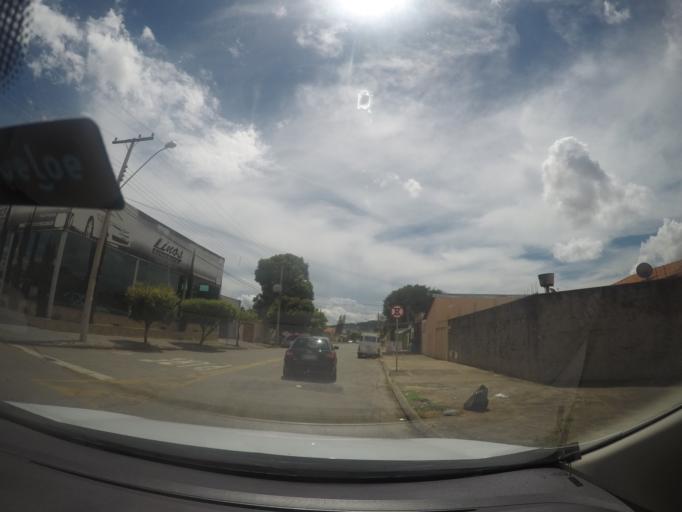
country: BR
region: Goias
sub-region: Goiania
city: Goiania
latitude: -16.6782
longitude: -49.3153
